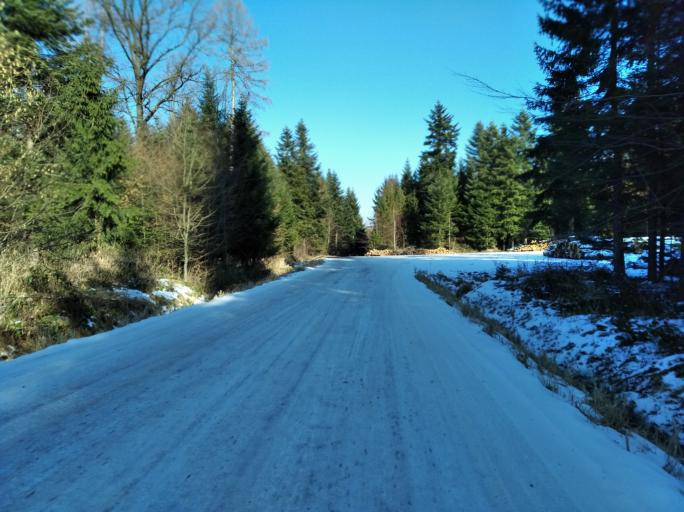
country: PL
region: Subcarpathian Voivodeship
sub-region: Powiat rzeszowski
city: Straszydle
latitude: 49.8688
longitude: 21.9736
